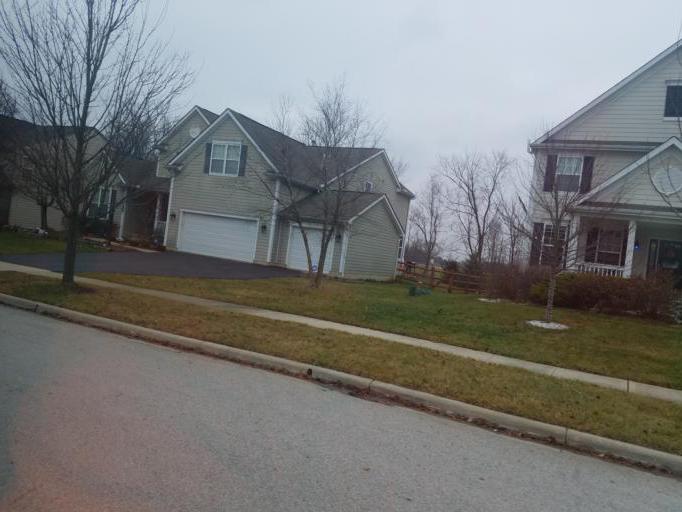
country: US
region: Ohio
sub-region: Franklin County
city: Westerville
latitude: 40.1941
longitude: -82.9234
